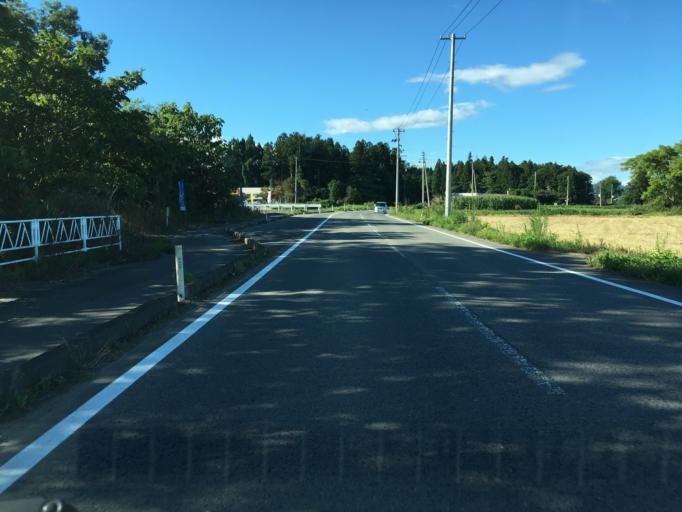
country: JP
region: Yamagata
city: Takahata
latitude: 37.9787
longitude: 140.1557
